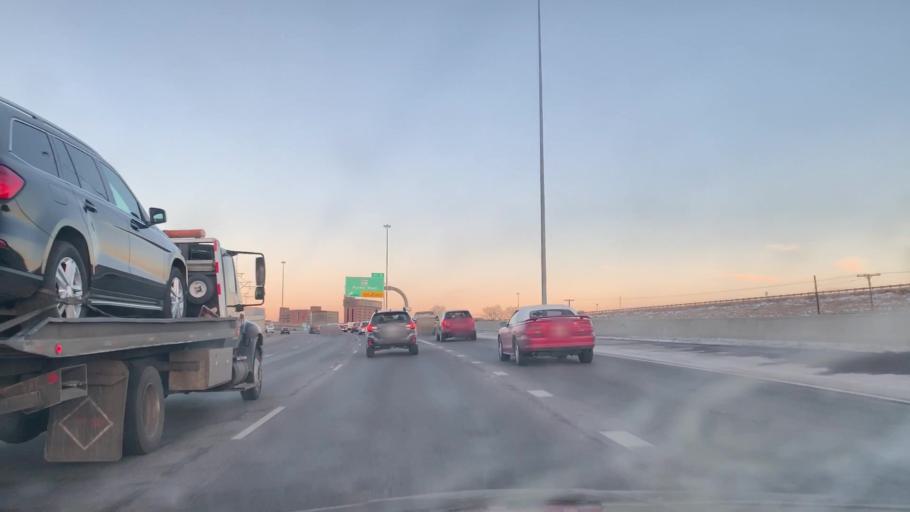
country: US
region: Colorado
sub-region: Adams County
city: Aurora
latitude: 39.6557
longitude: -104.8484
